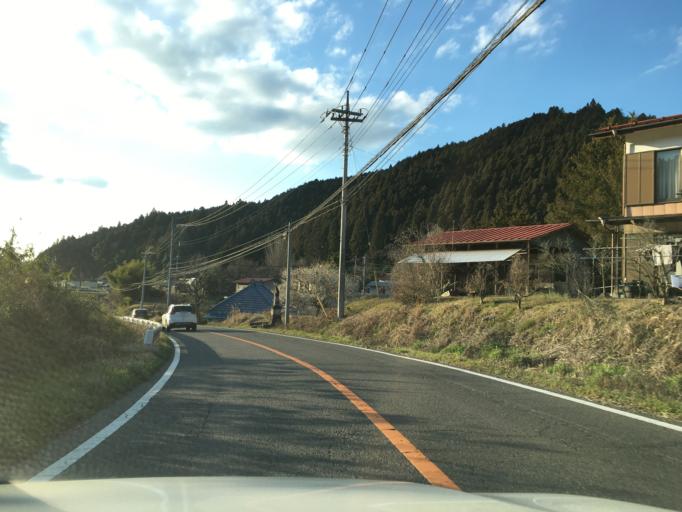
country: JP
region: Tochigi
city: Otawara
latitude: 36.8648
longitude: 140.1665
